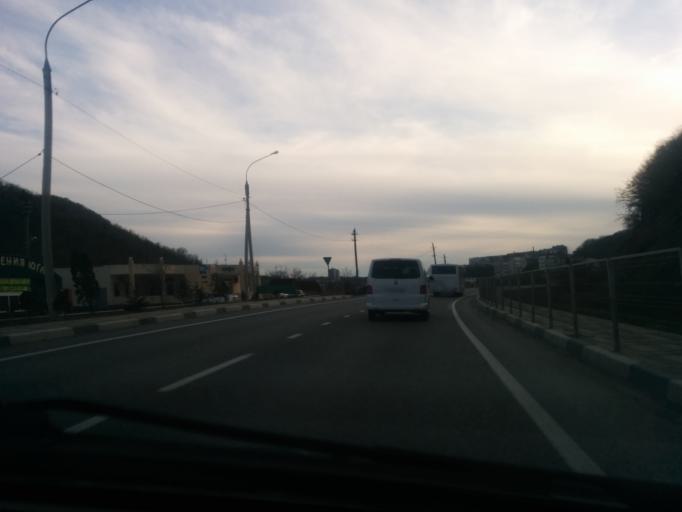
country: RU
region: Krasnodarskiy
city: Ol'ginka
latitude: 44.2074
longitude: 38.8912
